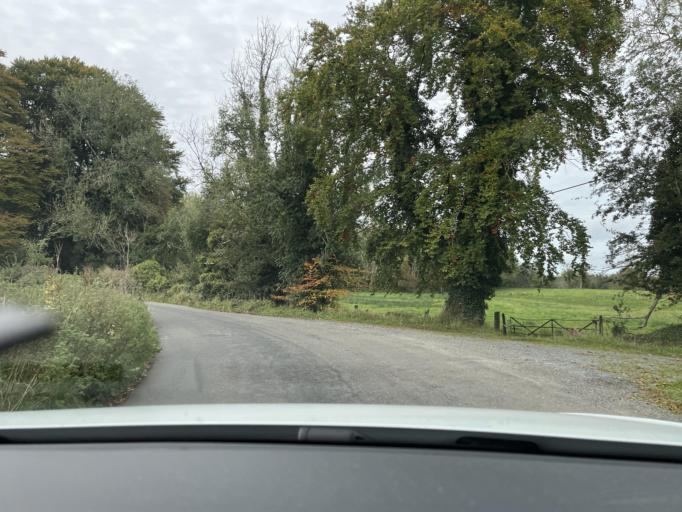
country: IE
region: Connaught
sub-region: Roscommon
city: Boyle
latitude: 53.9773
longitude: -8.2600
